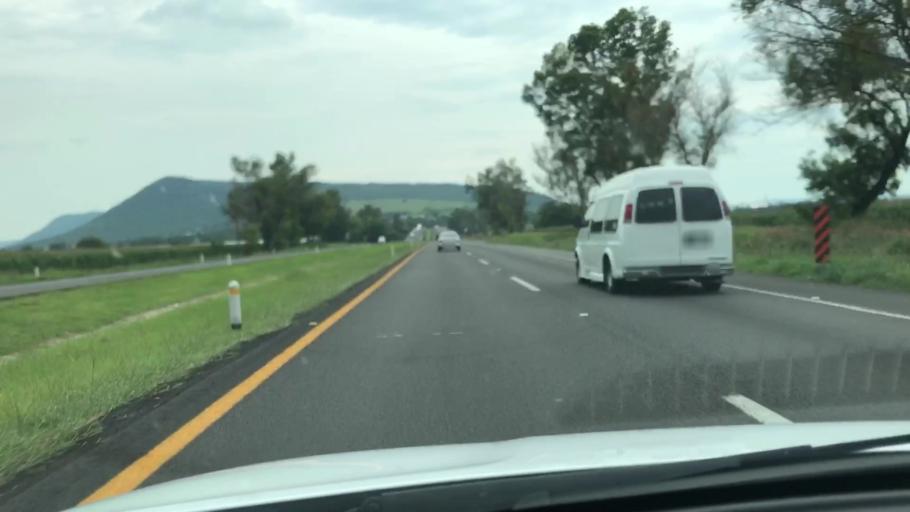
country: MX
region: Jalisco
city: Ocotlan
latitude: 20.3895
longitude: -102.7148
